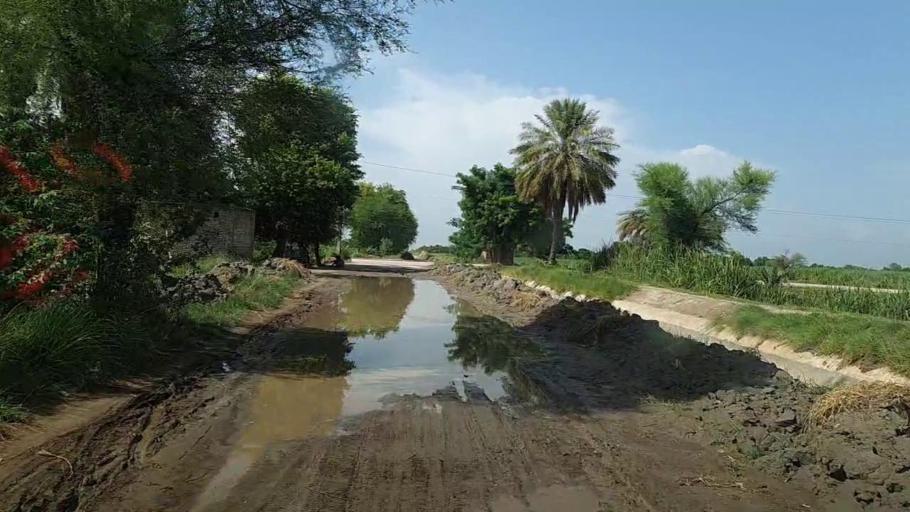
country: PK
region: Sindh
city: Bhiria
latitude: 26.8948
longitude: 68.2370
